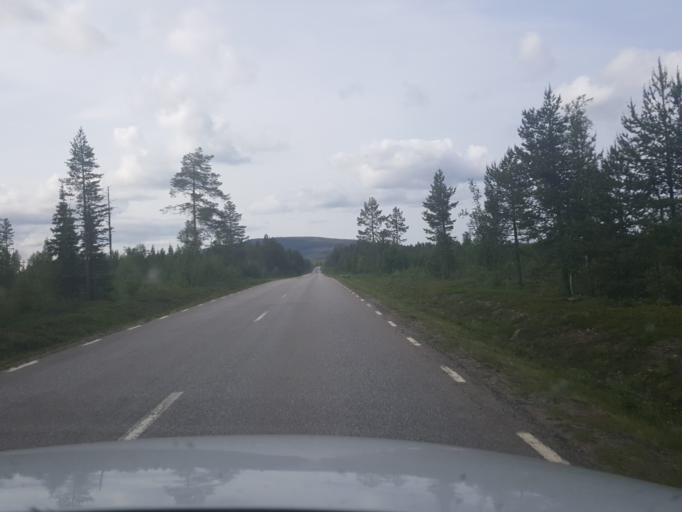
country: SE
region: Norrbotten
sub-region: Arjeplogs Kommun
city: Arjeplog
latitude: 65.6187
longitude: 18.0799
